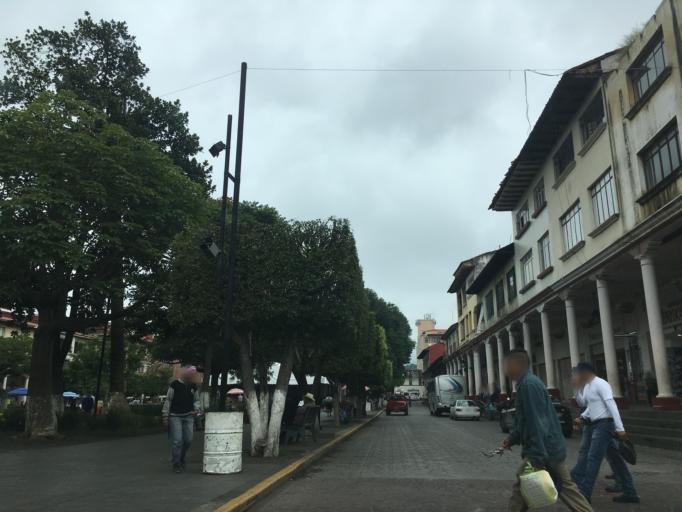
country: MX
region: Michoacan
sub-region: Uruapan
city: Uruapan
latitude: 19.4210
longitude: -102.0622
